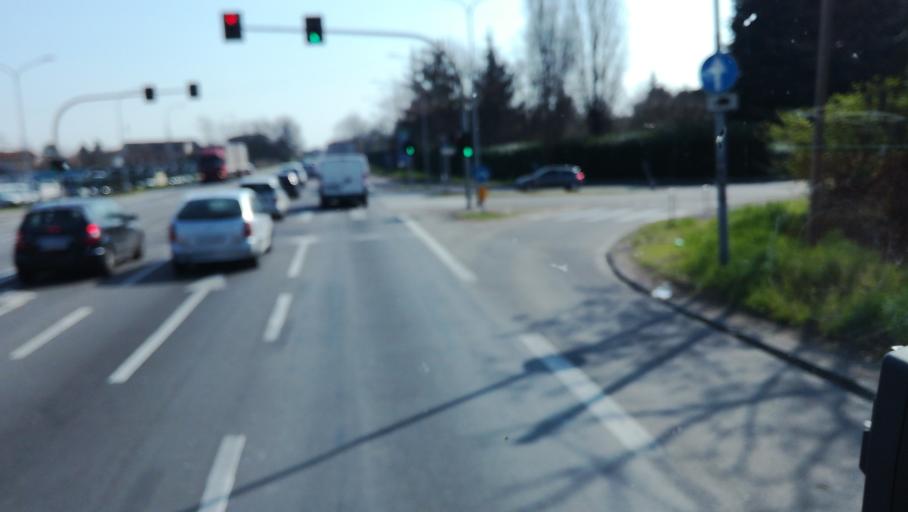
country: IT
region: Lombardy
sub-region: Citta metropolitana di Milano
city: Passirana
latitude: 45.5403
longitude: 9.0259
